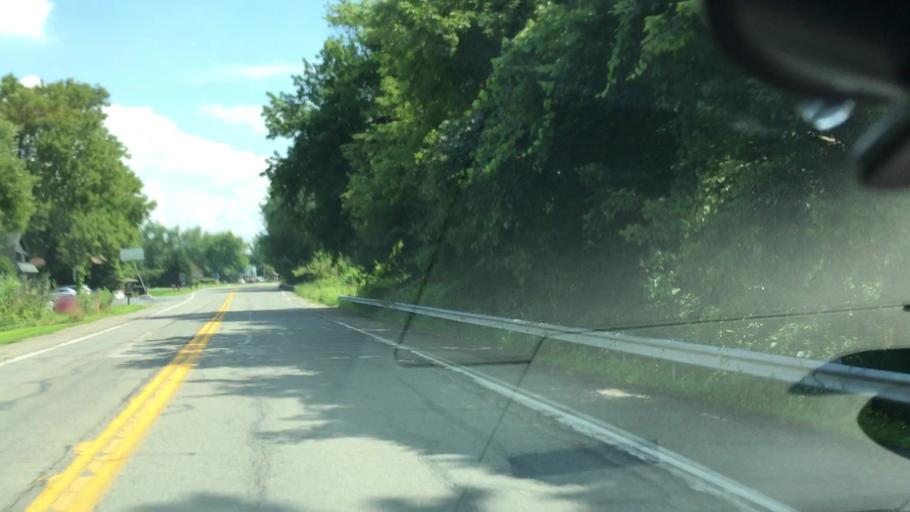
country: US
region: Pennsylvania
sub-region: Perry County
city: Marysville
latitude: 40.3345
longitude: -76.9038
